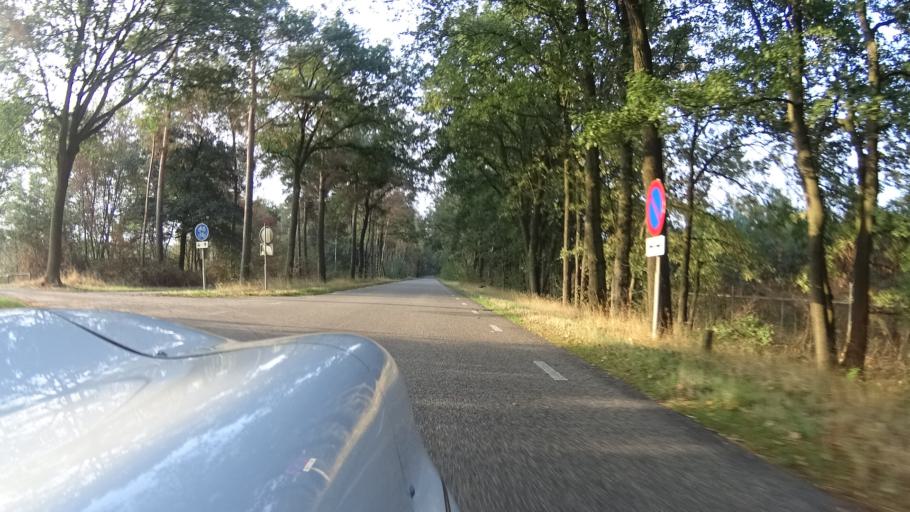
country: NL
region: Limburg
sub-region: Gemeente Venlo
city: Arcen
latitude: 51.4975
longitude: 6.2037
